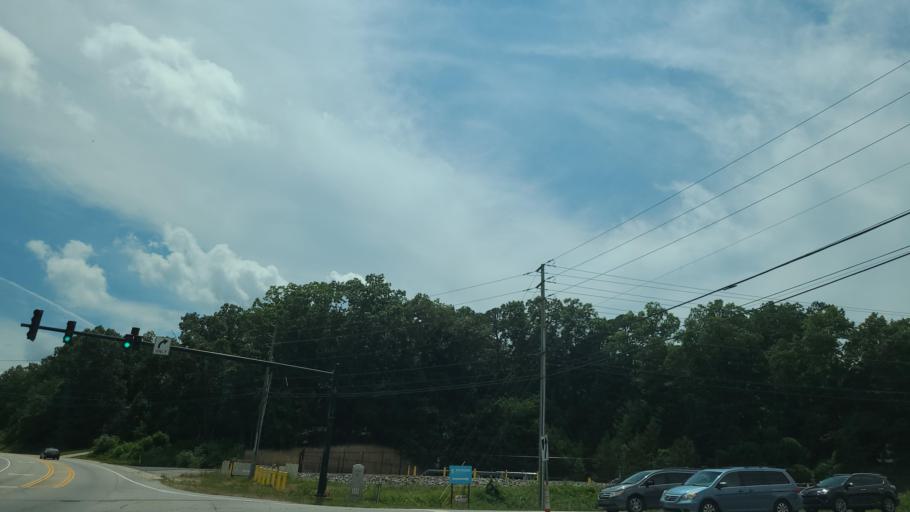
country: US
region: North Carolina
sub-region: Buncombe County
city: Avery Creek
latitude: 35.4801
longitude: -82.5653
